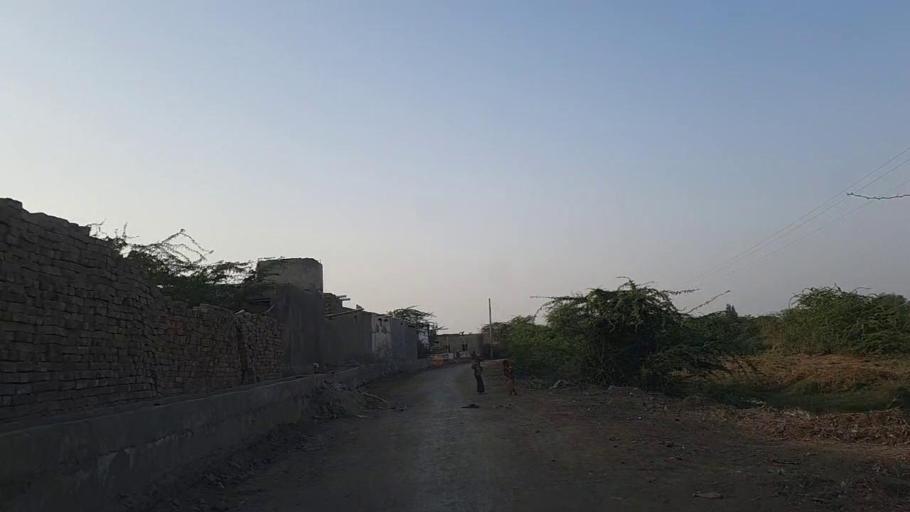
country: PK
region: Sindh
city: Pithoro
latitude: 25.5088
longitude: 69.3880
